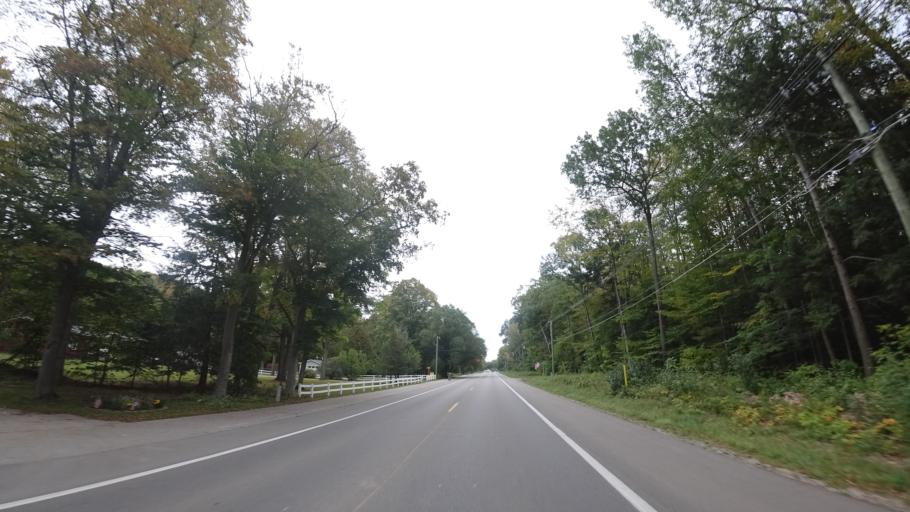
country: US
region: Michigan
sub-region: Emmet County
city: Petoskey
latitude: 45.4300
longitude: -84.9276
